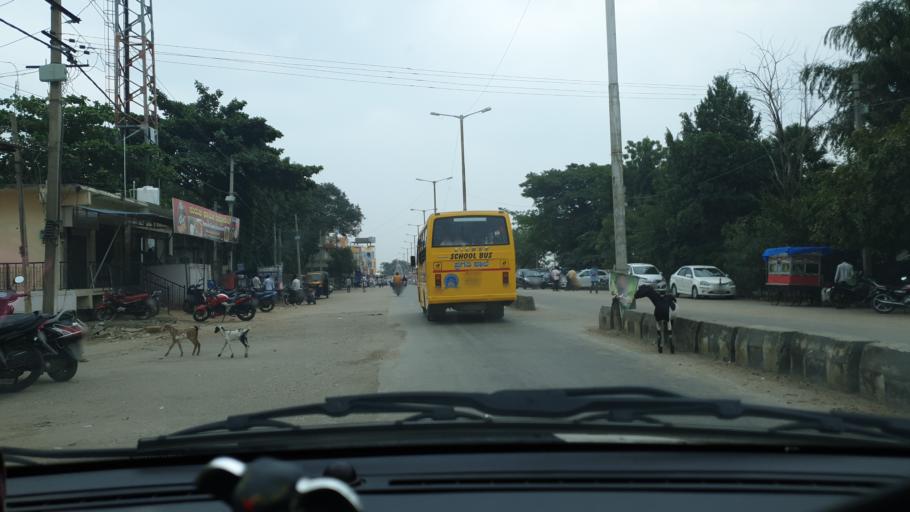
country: IN
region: Karnataka
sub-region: Yadgir
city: Gurmatkal
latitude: 16.8732
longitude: 77.3901
